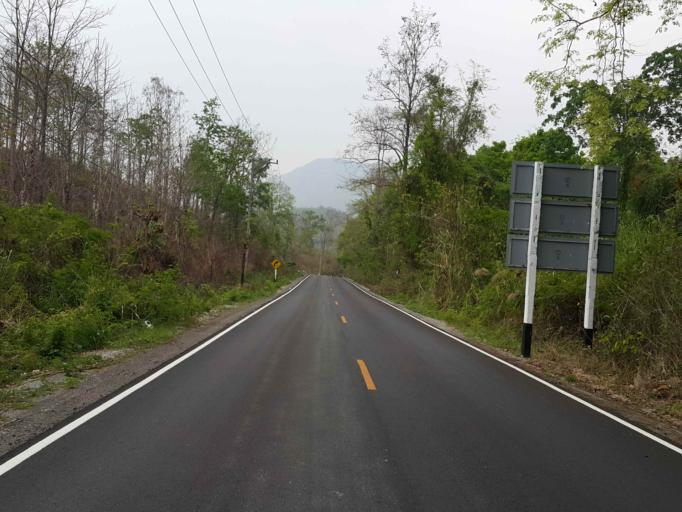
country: TH
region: Chiang Mai
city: Mae Taeng
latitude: 19.1060
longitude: 99.0786
